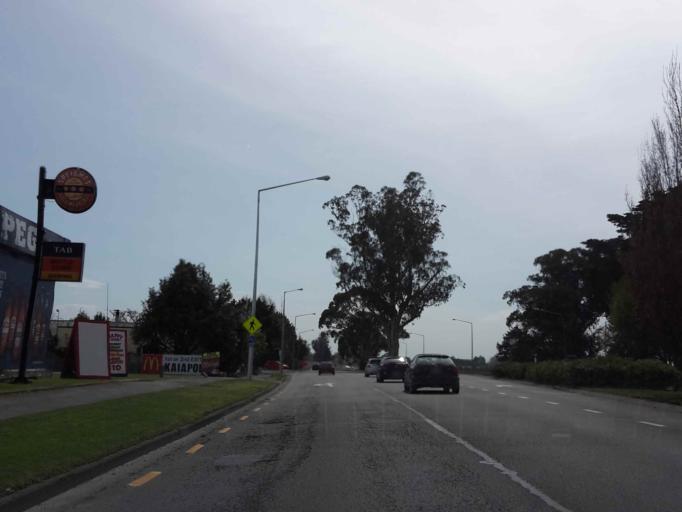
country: NZ
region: Canterbury
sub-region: Waimakariri District
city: Kaiapoi
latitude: -43.4382
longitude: 172.6369
